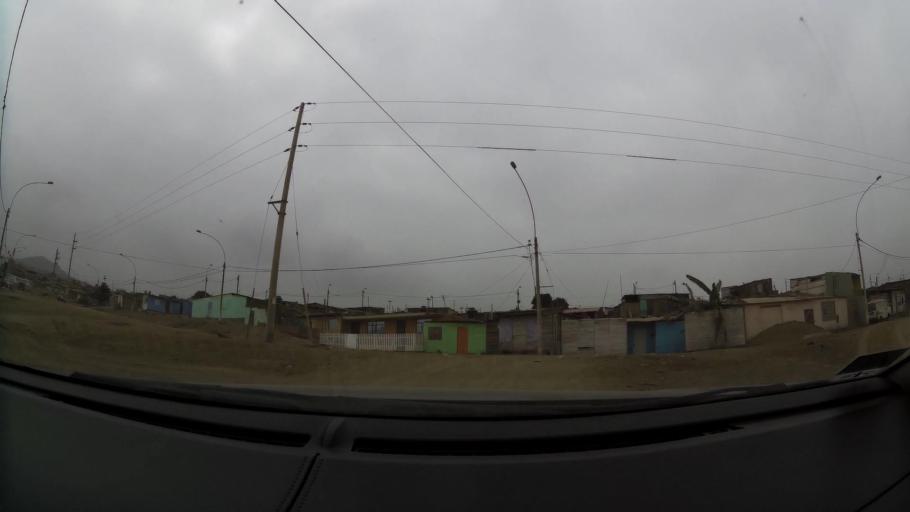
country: PE
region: Lima
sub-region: Lima
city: Santa Rosa
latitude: -11.8446
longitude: -77.1573
